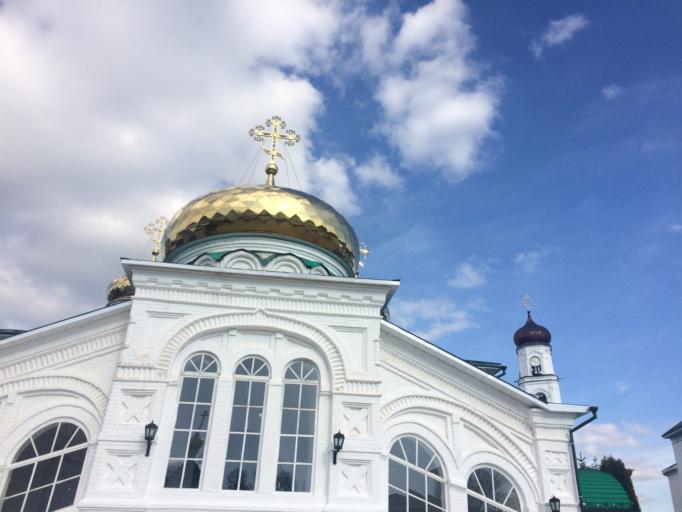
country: RU
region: Tatarstan
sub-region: Zelenodol'skiy Rayon
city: Vasil'yevo
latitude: 55.9020
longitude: 48.7287
